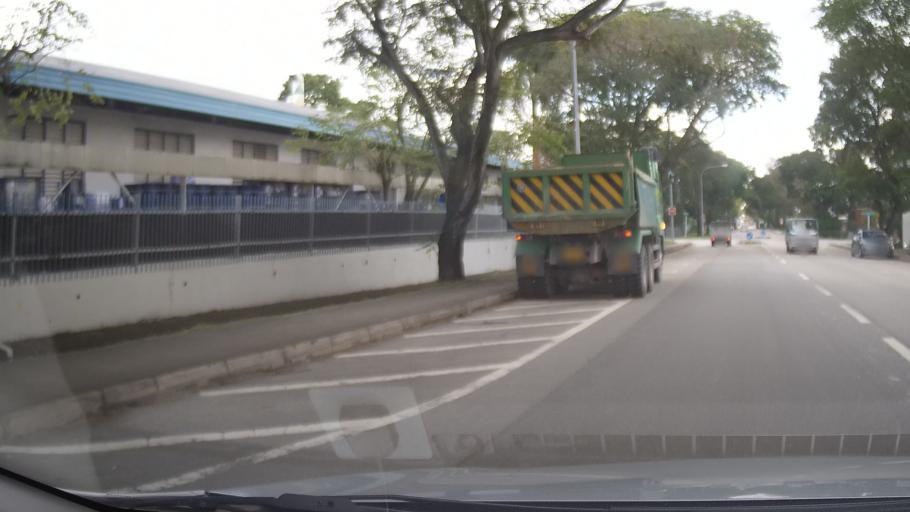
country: MY
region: Johor
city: Johor Bahru
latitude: 1.3237
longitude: 103.6935
